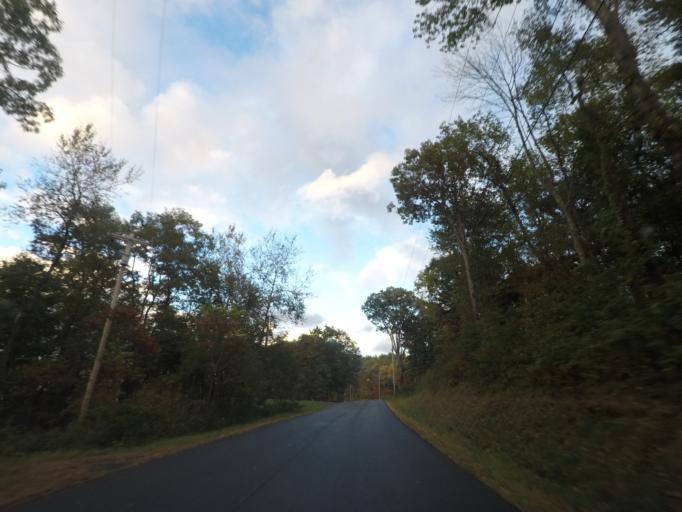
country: US
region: New York
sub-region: Rensselaer County
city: Nassau
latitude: 42.5564
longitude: -73.6181
